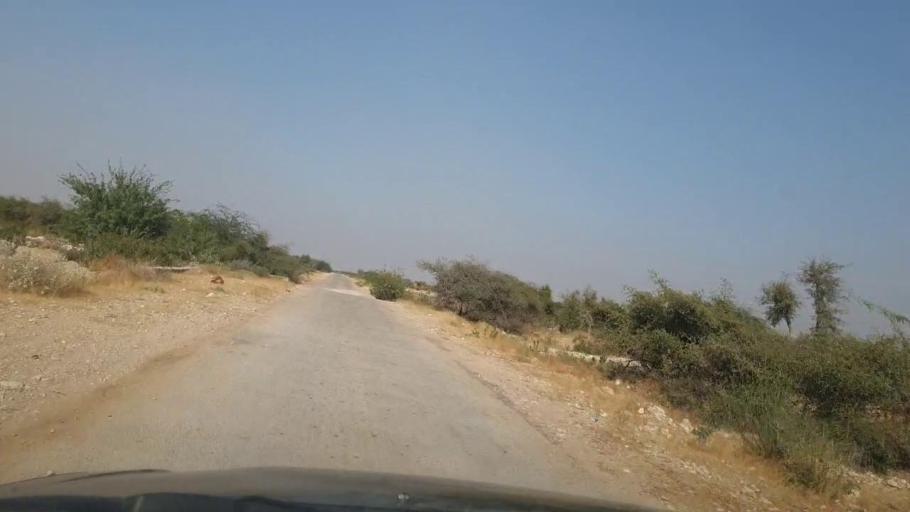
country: PK
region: Sindh
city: Jamshoro
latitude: 25.5414
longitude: 67.8258
